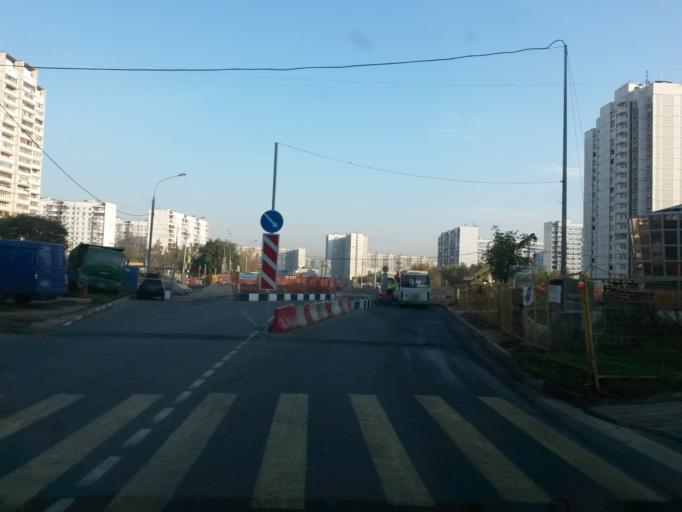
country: RU
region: Moscow
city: Orekhovo-Borisovo
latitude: 55.6258
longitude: 37.7424
